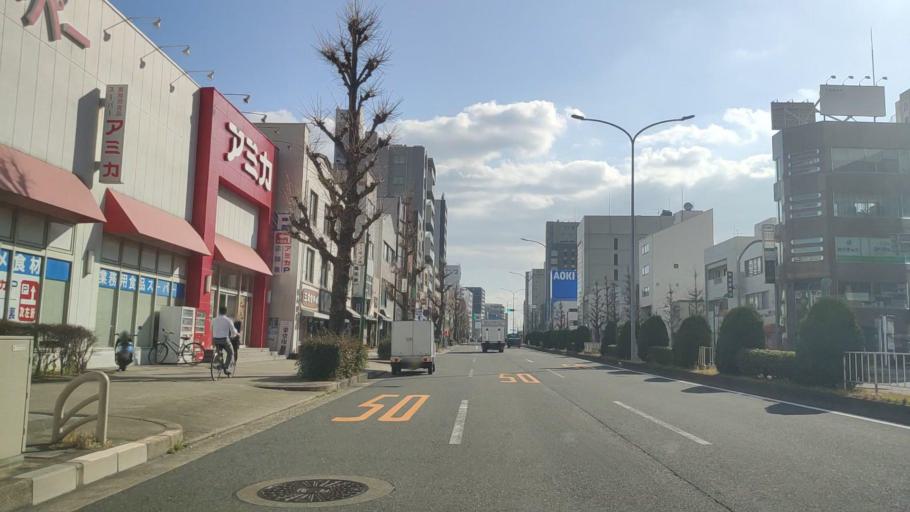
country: JP
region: Aichi
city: Nagoya-shi
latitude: 35.1577
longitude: 136.9019
